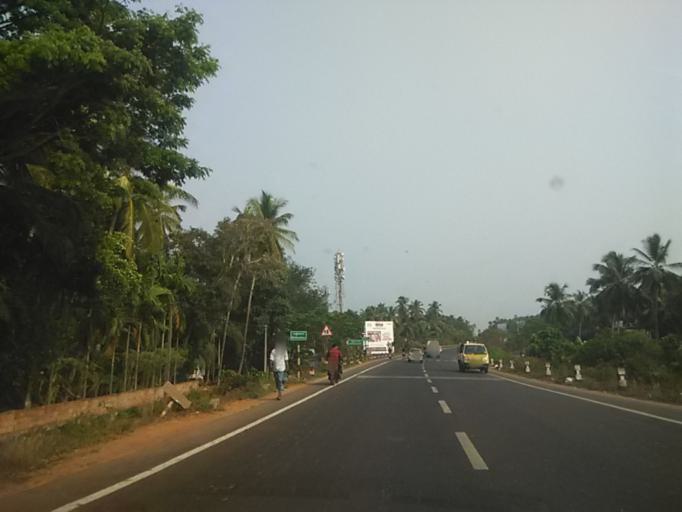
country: IN
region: Kerala
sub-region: Kozhikode
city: Kozhikode
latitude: 11.3122
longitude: 75.7822
